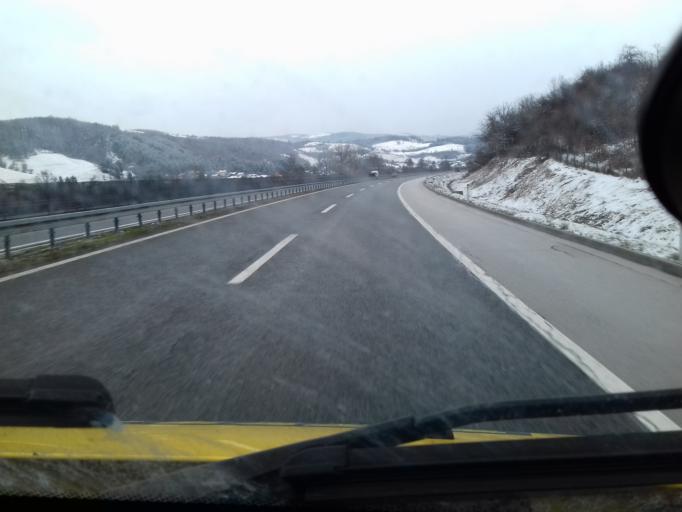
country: BA
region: Federation of Bosnia and Herzegovina
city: Visoko
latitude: 43.9929
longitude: 18.2129
